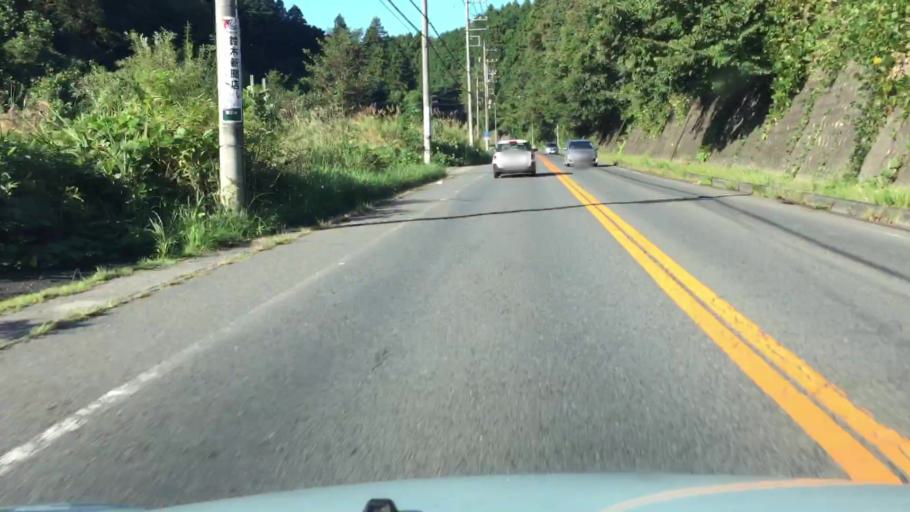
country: JP
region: Tochigi
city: Ujiie
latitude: 36.7076
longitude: 140.0209
